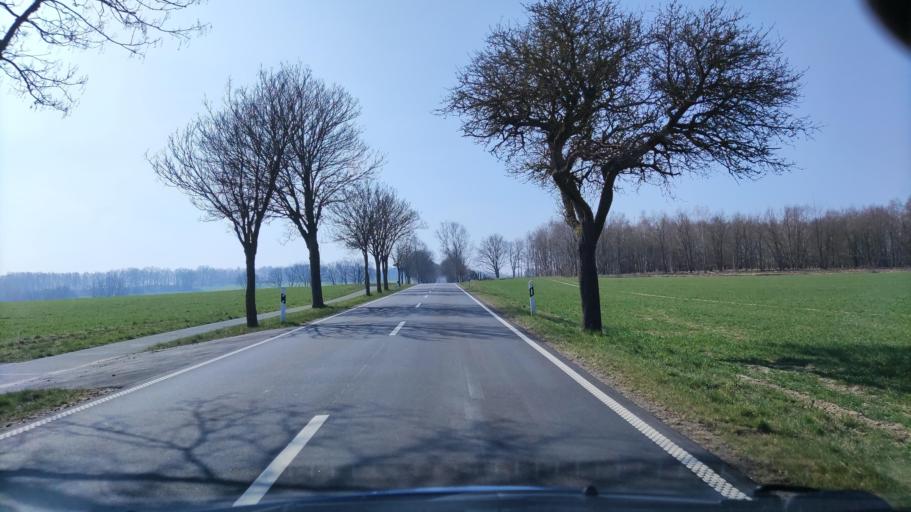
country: DE
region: Lower Saxony
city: Clenze
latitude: 52.9535
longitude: 10.9696
